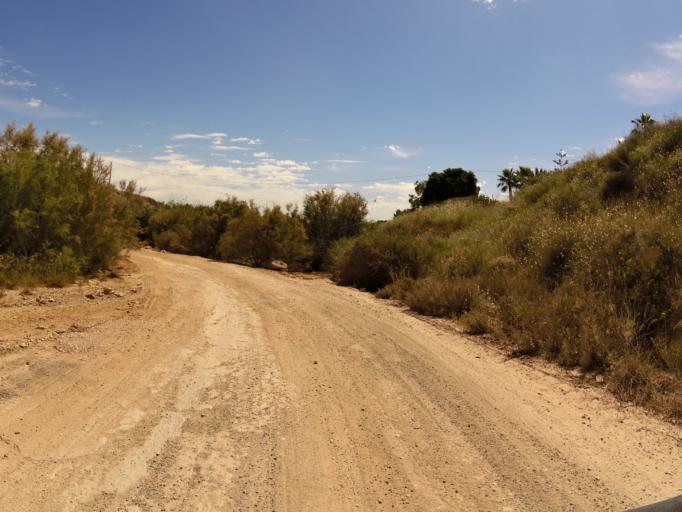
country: ES
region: Valencia
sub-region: Provincia de Alicante
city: Agost
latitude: 38.3969
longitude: -0.6091
